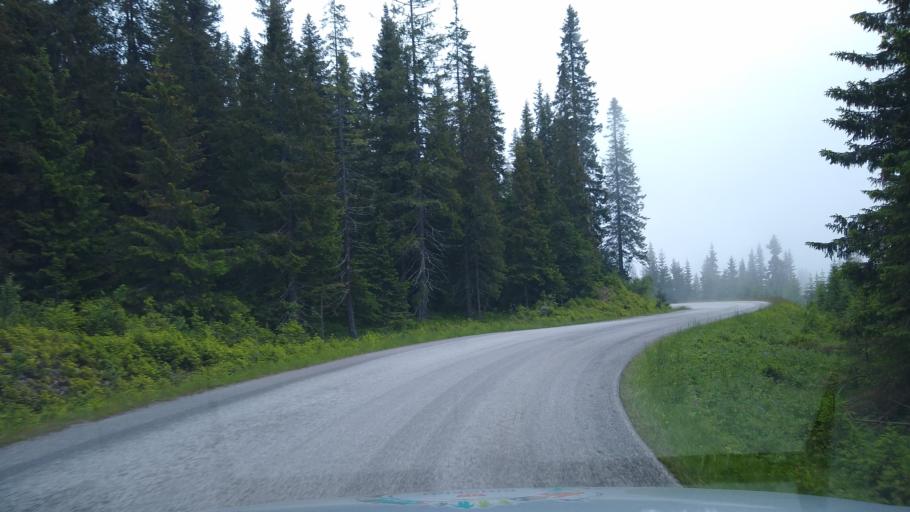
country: NO
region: Oppland
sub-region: Ringebu
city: Ringebu
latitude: 61.4919
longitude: 10.1323
